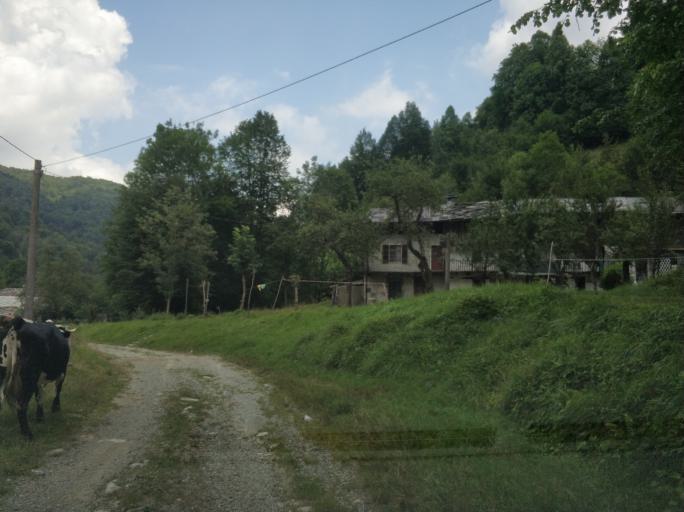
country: IT
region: Piedmont
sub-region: Provincia di Torino
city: Viu
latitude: 45.2133
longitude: 7.3943
